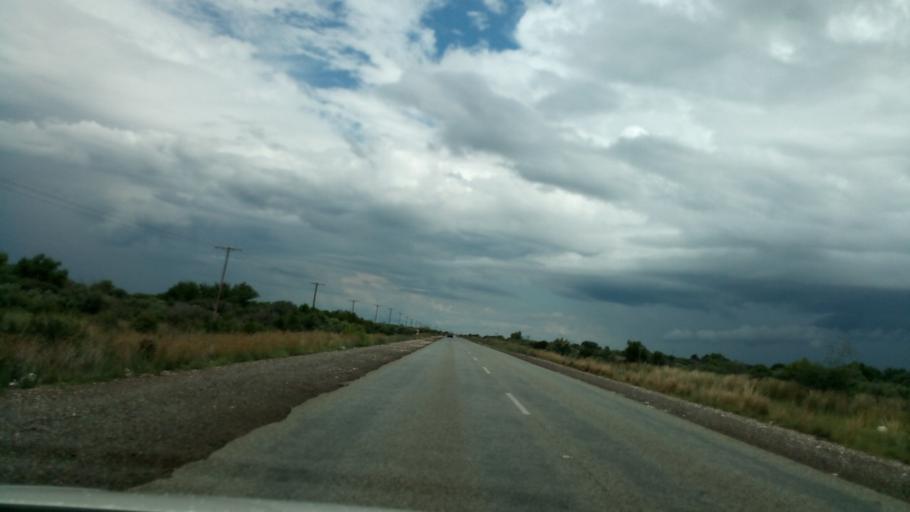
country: ZA
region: Northern Cape
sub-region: Siyanda District Municipality
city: Danielskuil
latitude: -28.2545
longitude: 24.0464
